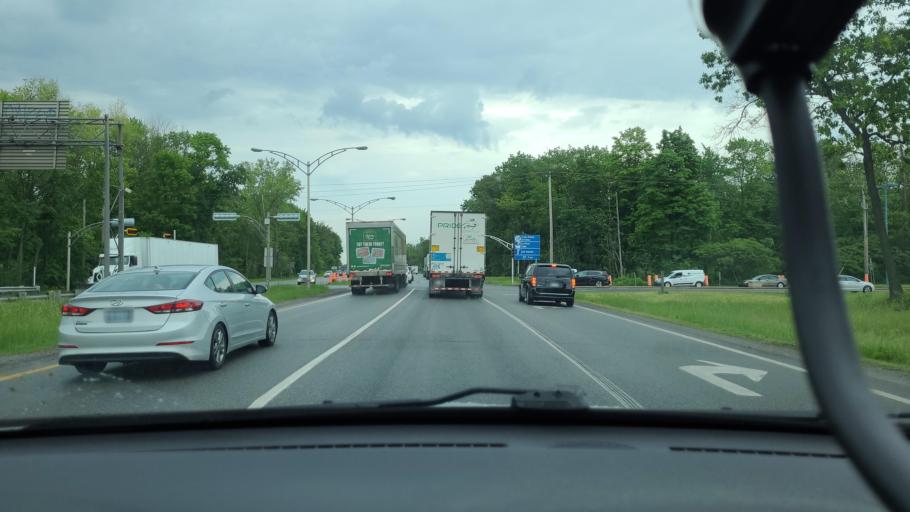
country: CA
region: Quebec
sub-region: Monteregie
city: Pincourt
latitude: 45.3879
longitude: -73.9819
